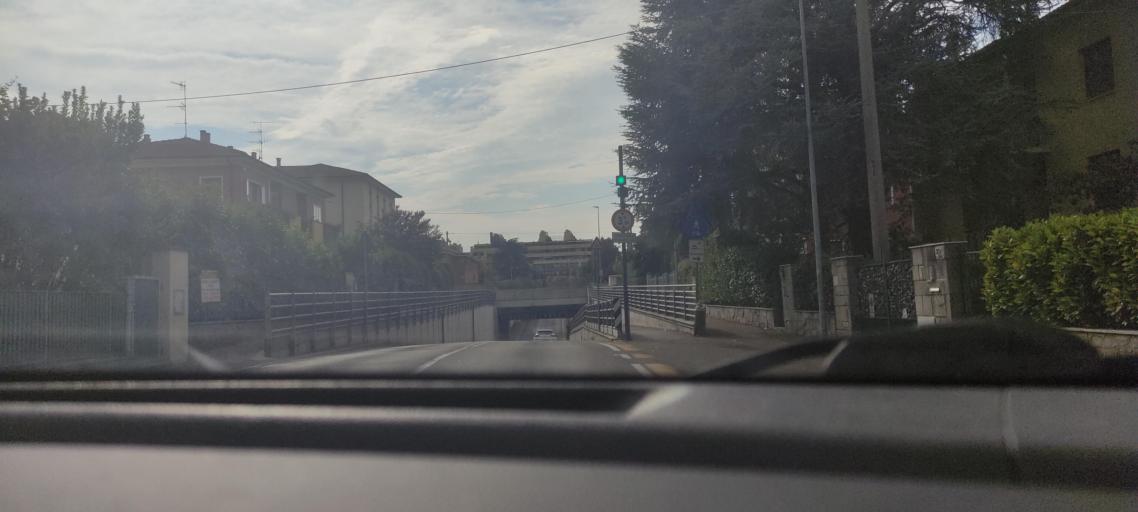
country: IT
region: Emilia-Romagna
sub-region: Provincia di Bologna
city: Progresso
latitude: 44.5742
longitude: 11.3674
